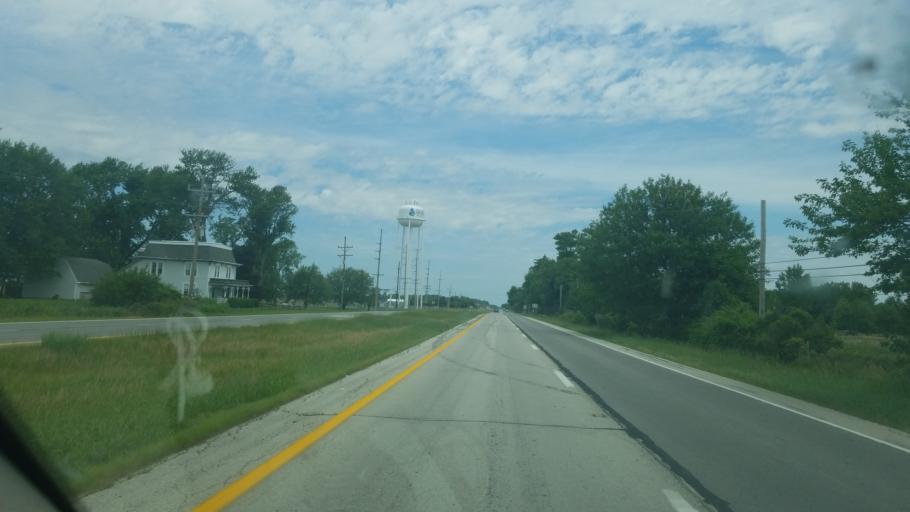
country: US
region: Ohio
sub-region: Wood County
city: North Baltimore
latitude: 41.2664
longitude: -83.6501
